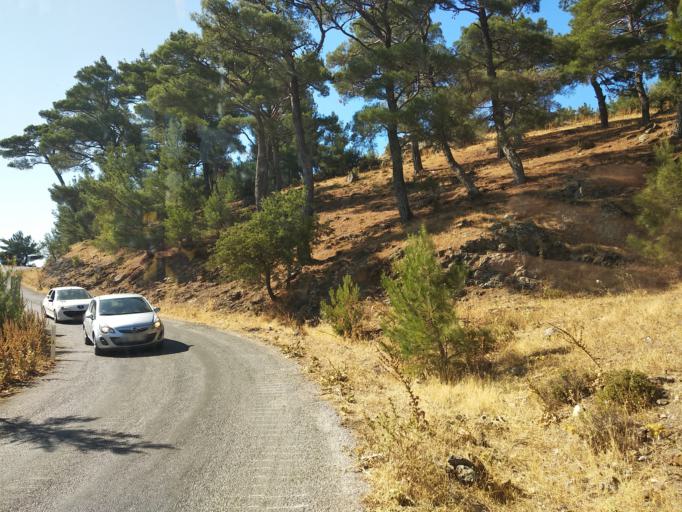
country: TR
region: Izmir
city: Gaziemir
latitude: 38.2988
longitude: 26.9971
